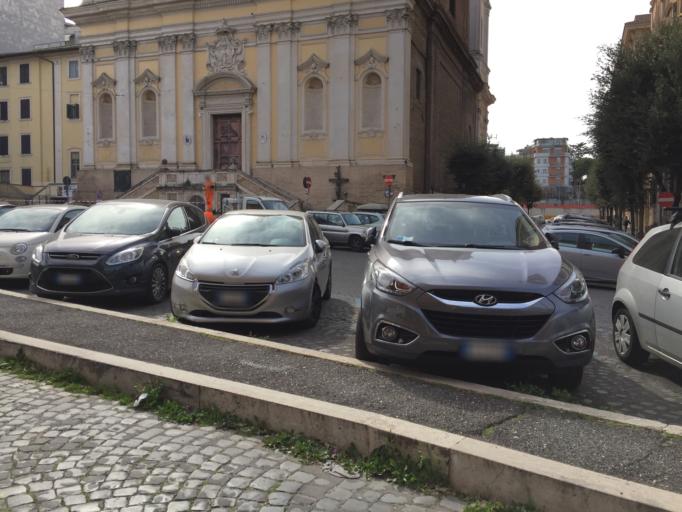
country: VA
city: Vatican City
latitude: 41.8980
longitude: 12.4549
